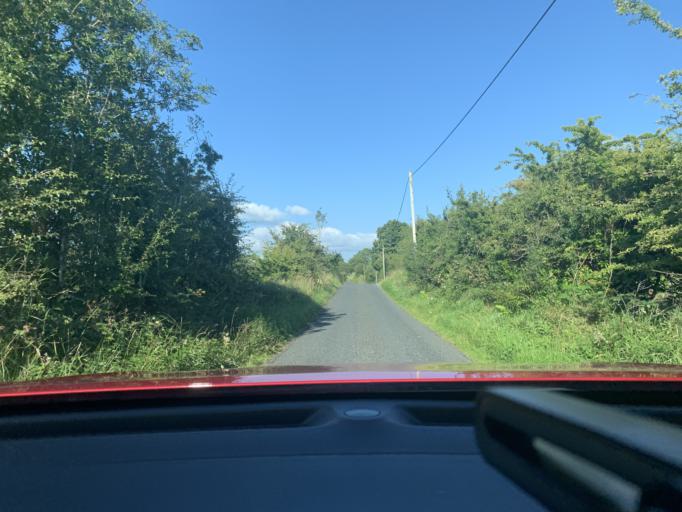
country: IE
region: Connaught
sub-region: Sligo
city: Strandhill
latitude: 54.1630
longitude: -8.6388
